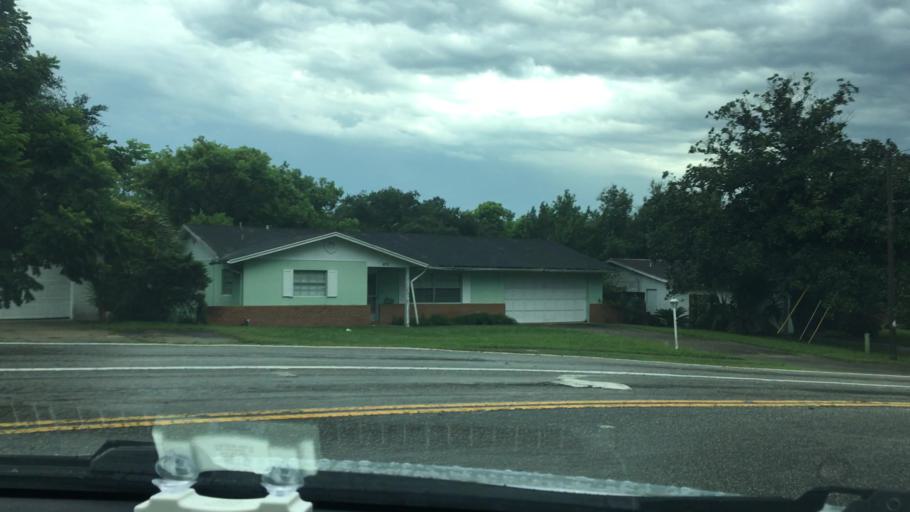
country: US
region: Florida
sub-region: Volusia County
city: Deltona
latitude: 28.9101
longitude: -81.2598
